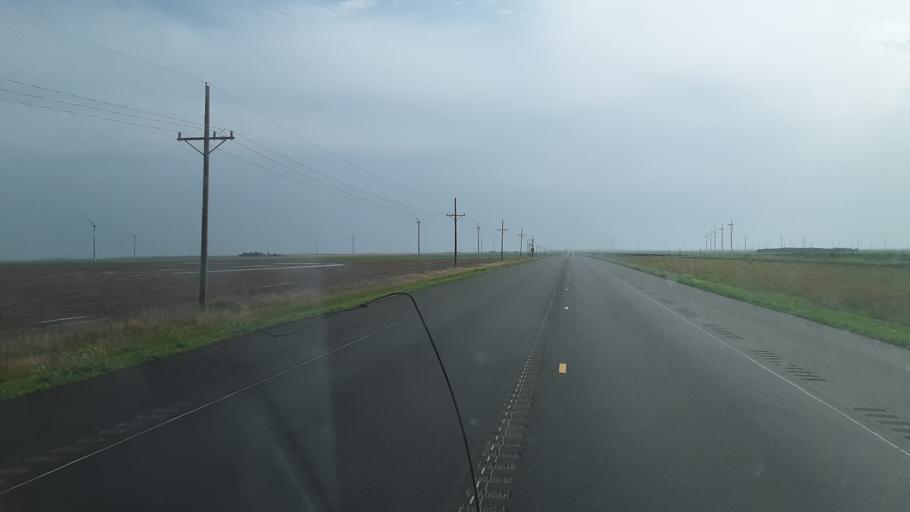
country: US
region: Kansas
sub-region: Ford County
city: Dodge City
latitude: 37.8012
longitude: -99.8554
